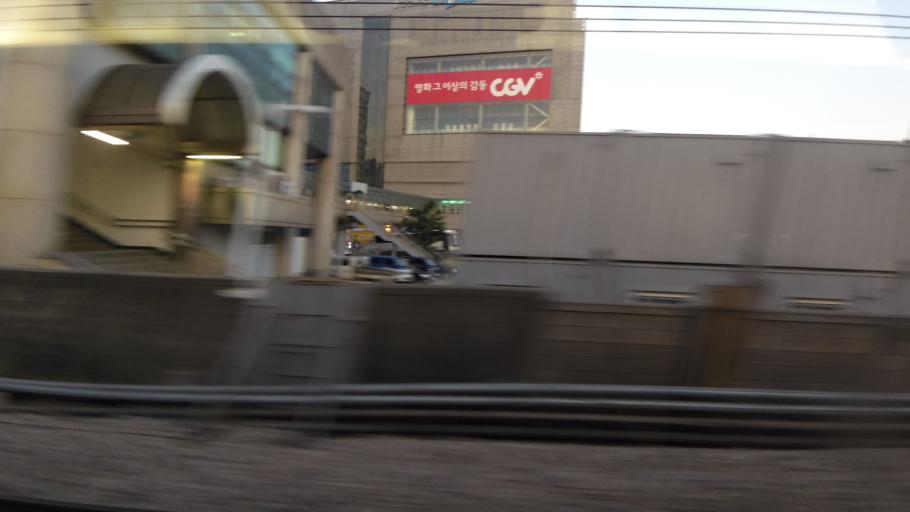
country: KR
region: Gyeonggi-do
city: Kwangmyong
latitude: 37.5020
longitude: 126.8814
